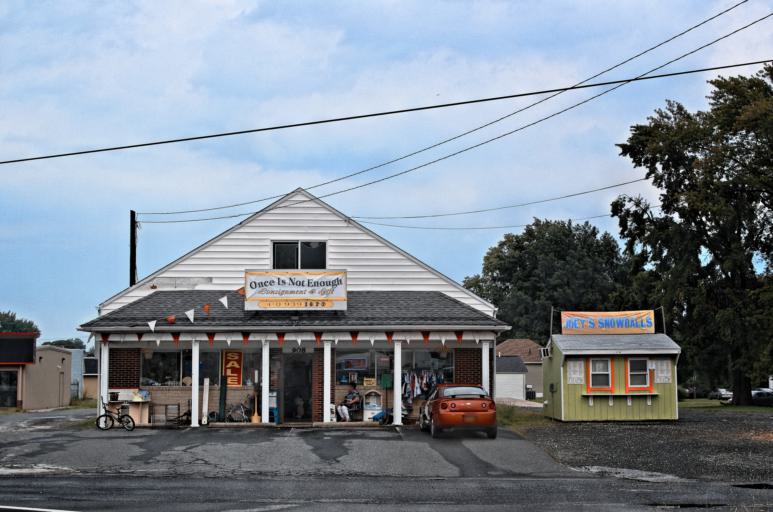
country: US
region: Maryland
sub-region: Harford County
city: Havre de Grace
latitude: 39.5521
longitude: -76.1023
